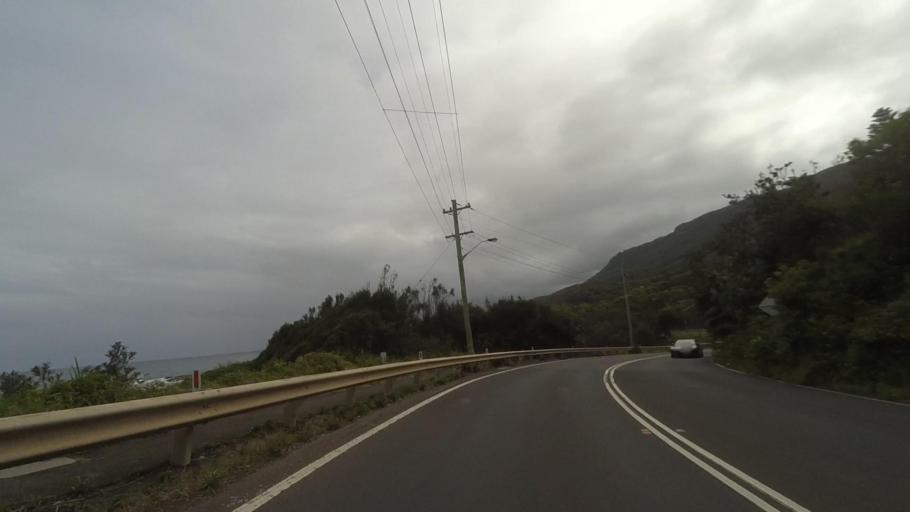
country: AU
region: New South Wales
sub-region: Wollongong
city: Bulli
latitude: -34.2855
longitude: 150.9503
